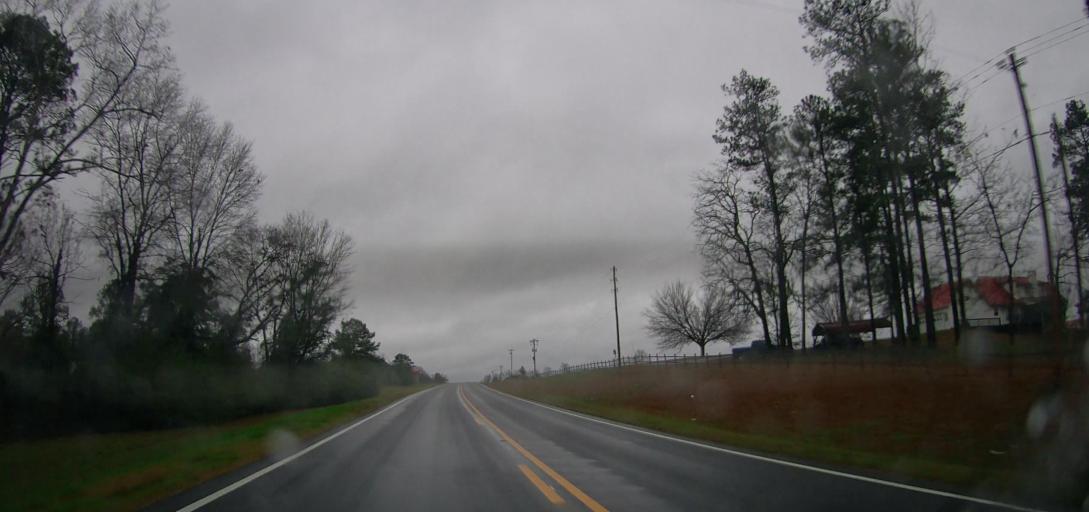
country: US
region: Alabama
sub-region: Chilton County
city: Thorsby
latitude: 32.7964
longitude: -86.9087
